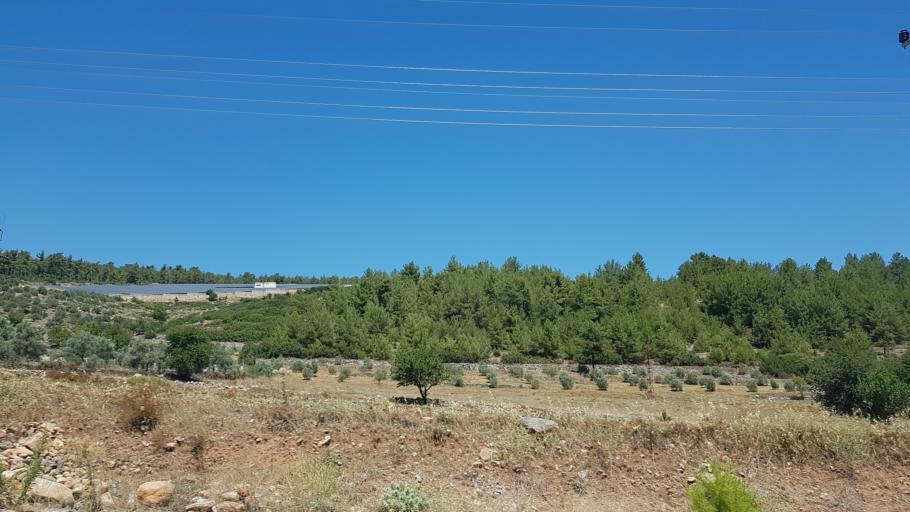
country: TR
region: Mugla
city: Turgut
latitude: 37.3086
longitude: 28.0151
